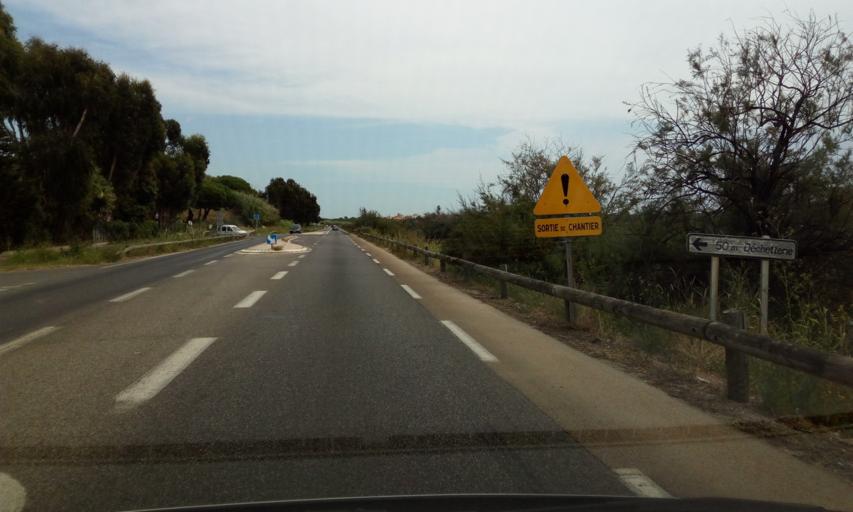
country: FR
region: Provence-Alpes-Cote d'Azur
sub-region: Departement du Var
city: Hyeres
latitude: 43.0809
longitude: 6.1345
